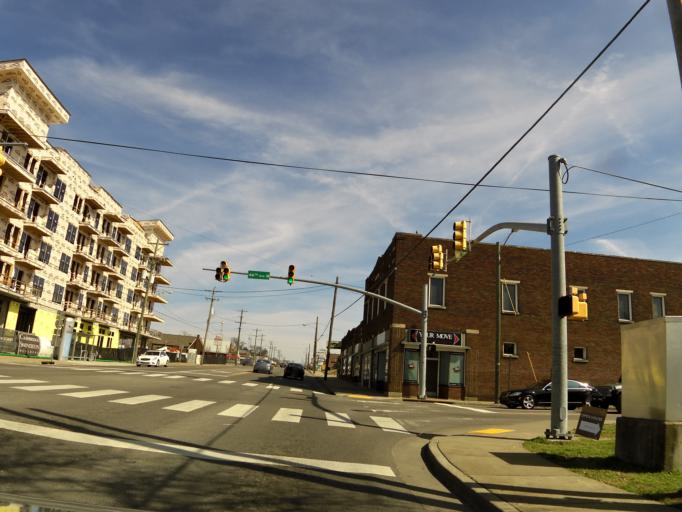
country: US
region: Tennessee
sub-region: Davidson County
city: Belle Meade
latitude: 36.1521
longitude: -86.8425
